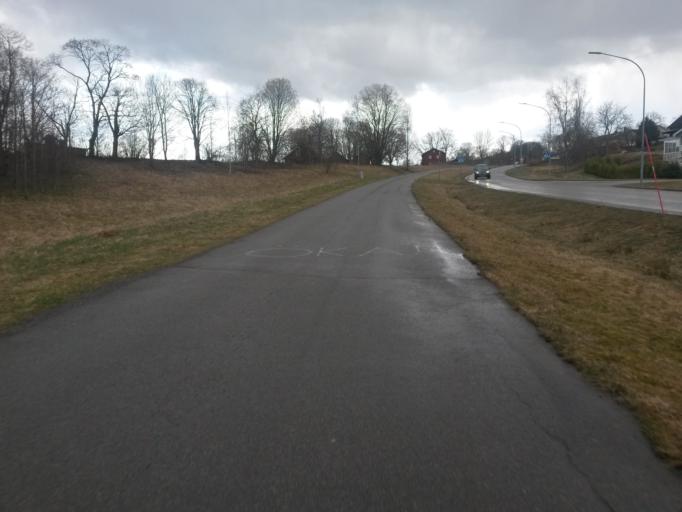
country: SE
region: OErebro
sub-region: Karlskoga Kommun
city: Karlskoga
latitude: 59.3116
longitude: 14.5145
